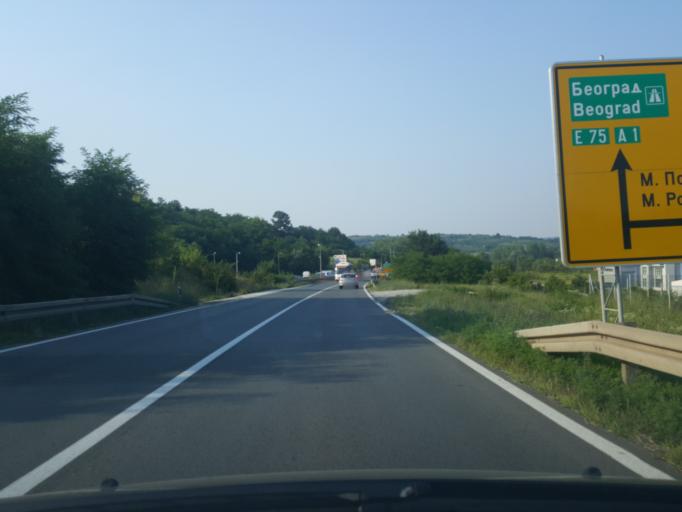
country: RS
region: Central Serbia
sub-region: Belgrade
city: Sopot
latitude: 44.5586
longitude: 20.6675
